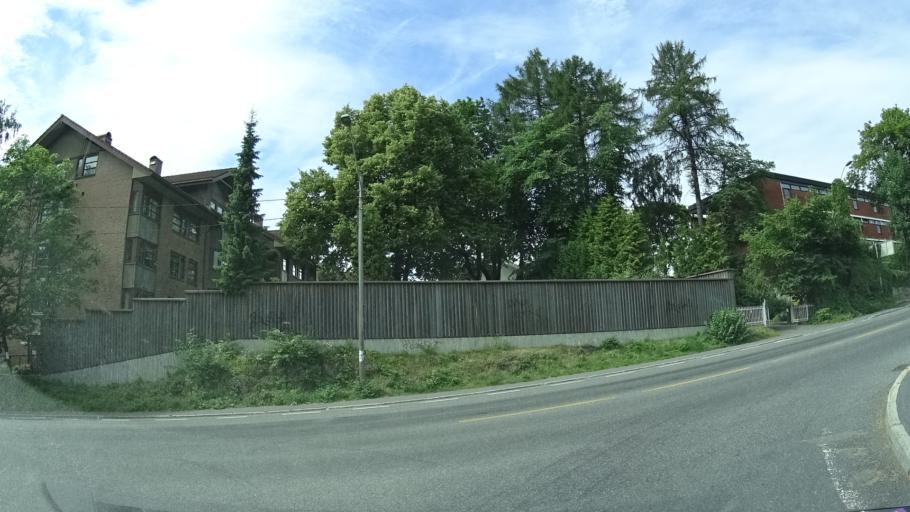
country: NO
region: Oslo
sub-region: Oslo
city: Oslo
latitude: 59.9524
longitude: 10.7612
